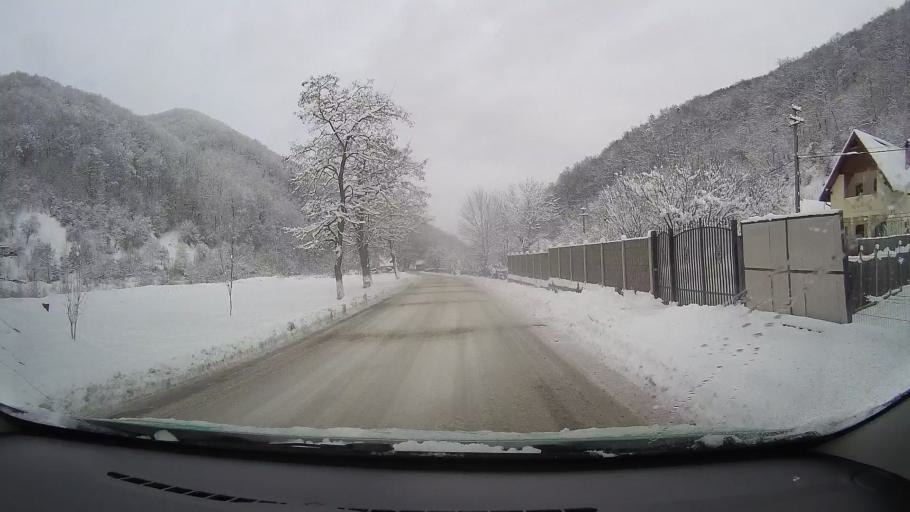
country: RO
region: Alba
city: Pianu de Sus
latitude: 45.8595
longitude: 23.4997
